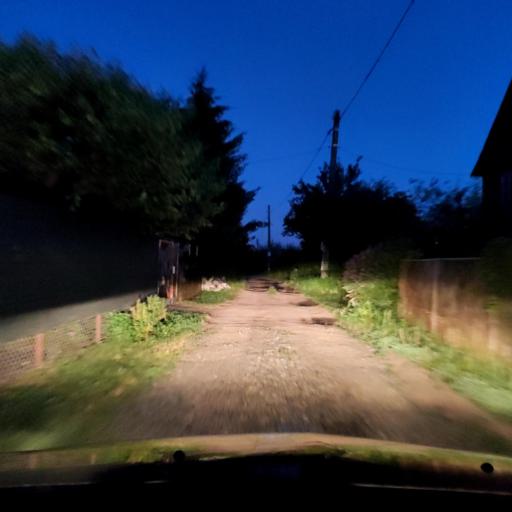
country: RU
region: Voronezj
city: Podgornoye
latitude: 51.8019
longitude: 39.2216
